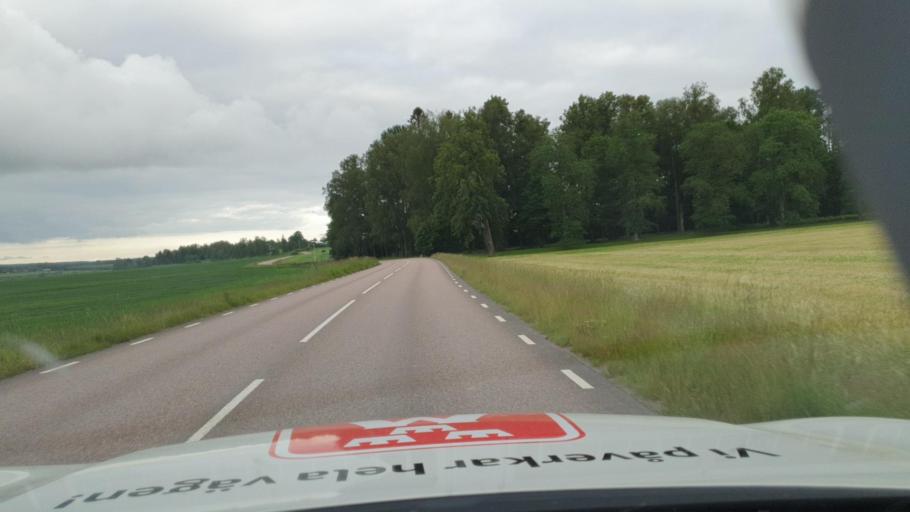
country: SE
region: Vaermland
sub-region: Kils Kommun
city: Kil
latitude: 59.5203
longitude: 13.3741
